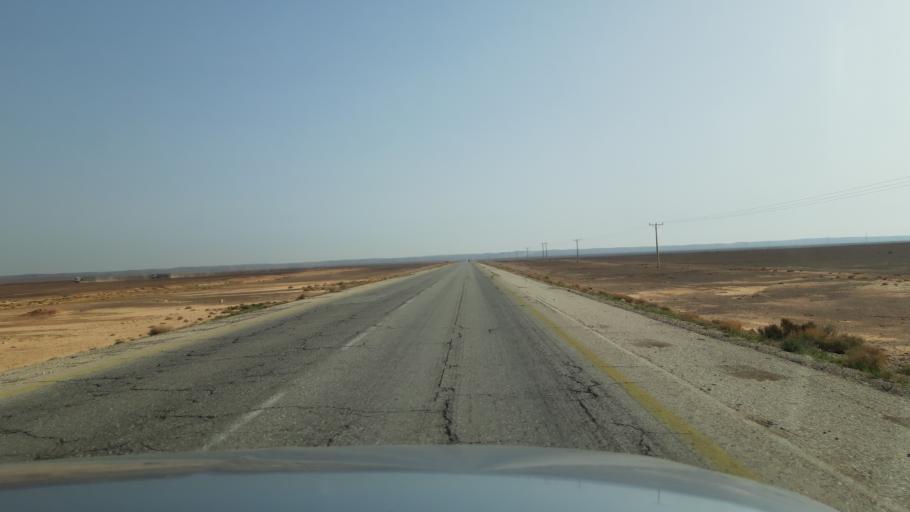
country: JO
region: Amman
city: Al Azraq ash Shamali
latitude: 31.8234
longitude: 36.6102
